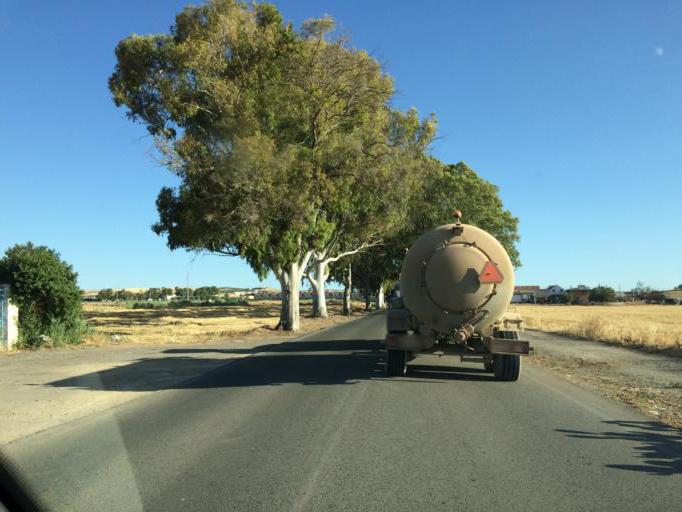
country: ES
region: Andalusia
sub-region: Provincia de Malaga
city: Campillos
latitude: 37.0358
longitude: -4.8573
